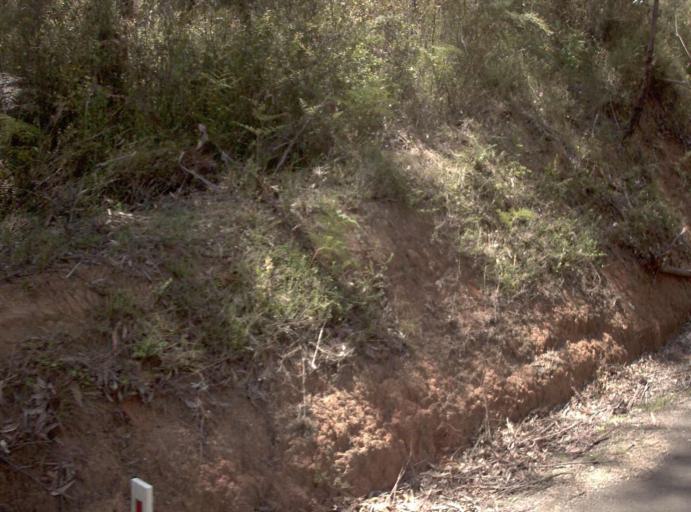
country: AU
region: New South Wales
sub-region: Bombala
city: Bombala
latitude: -37.5683
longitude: 149.0344
